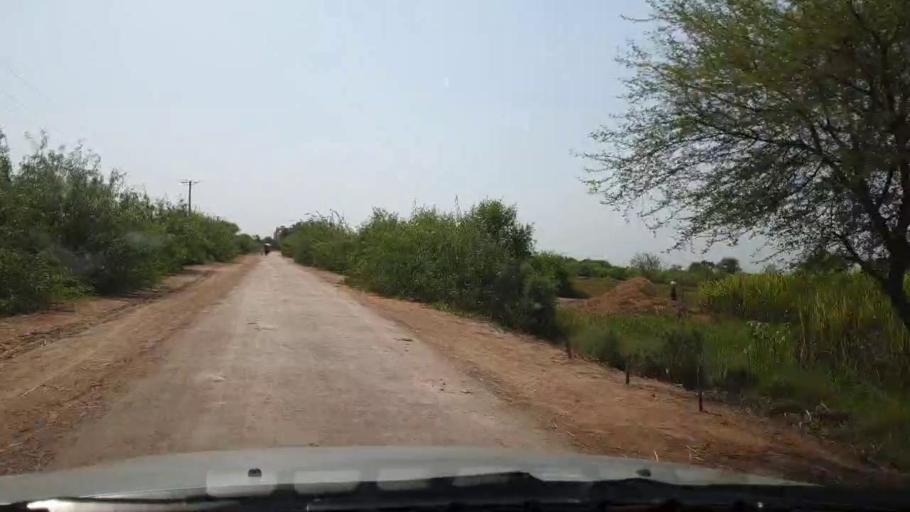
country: PK
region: Sindh
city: Tando Muhammad Khan
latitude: 25.1252
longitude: 68.6201
